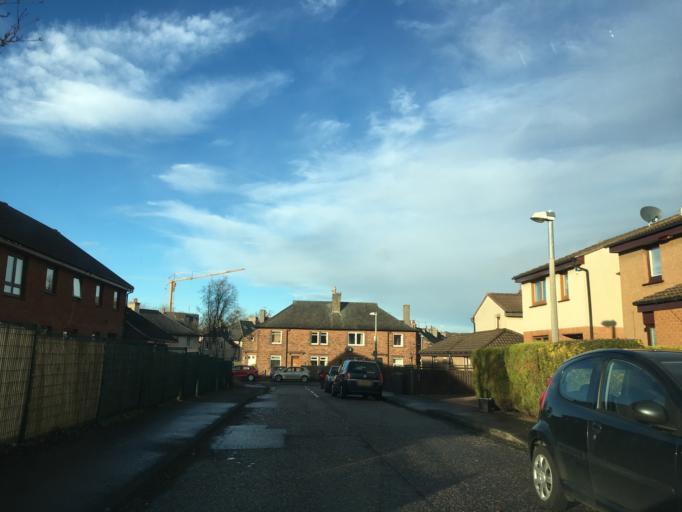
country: GB
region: Scotland
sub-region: Edinburgh
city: Colinton
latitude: 55.9284
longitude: -3.2512
